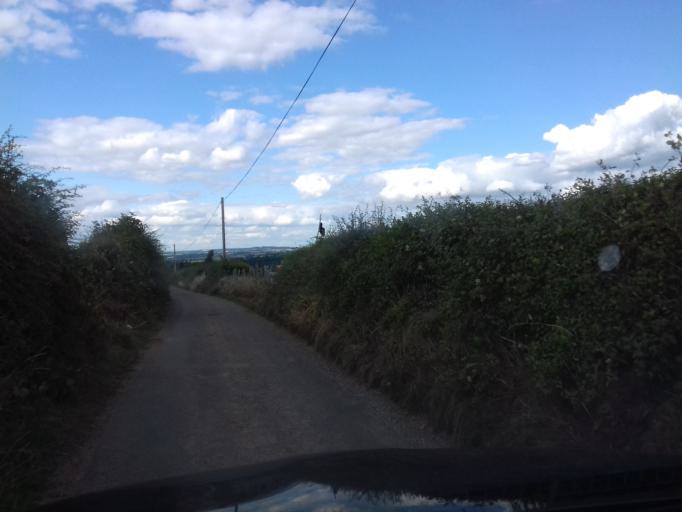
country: IE
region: Leinster
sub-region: Kilkenny
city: Graiguenamanagh
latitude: 52.5829
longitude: -7.0026
